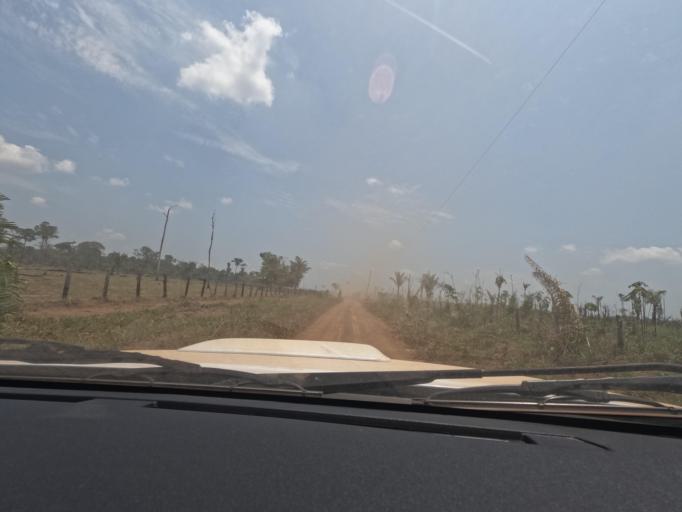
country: BR
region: Rondonia
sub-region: Porto Velho
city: Porto Velho
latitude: -8.6492
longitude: -64.1710
